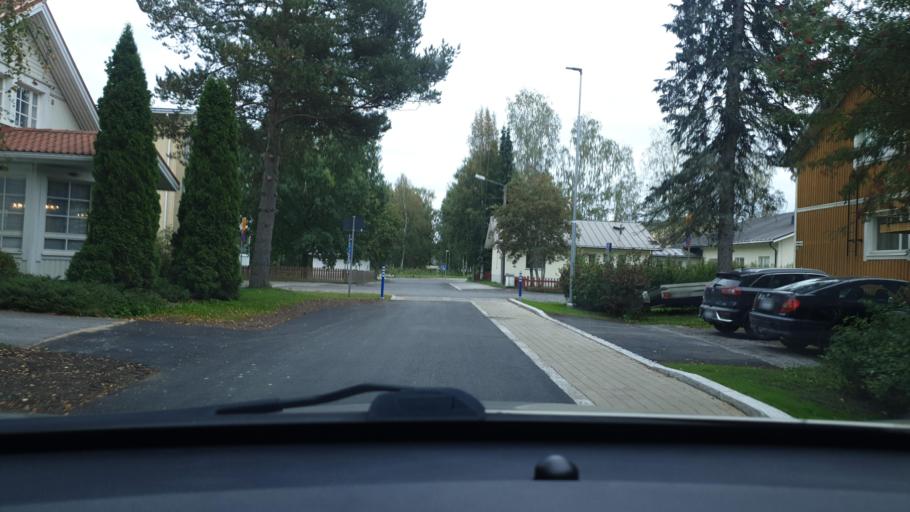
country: FI
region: Ostrobothnia
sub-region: Vaasa
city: Teeriniemi
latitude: 63.0946
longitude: 21.6757
